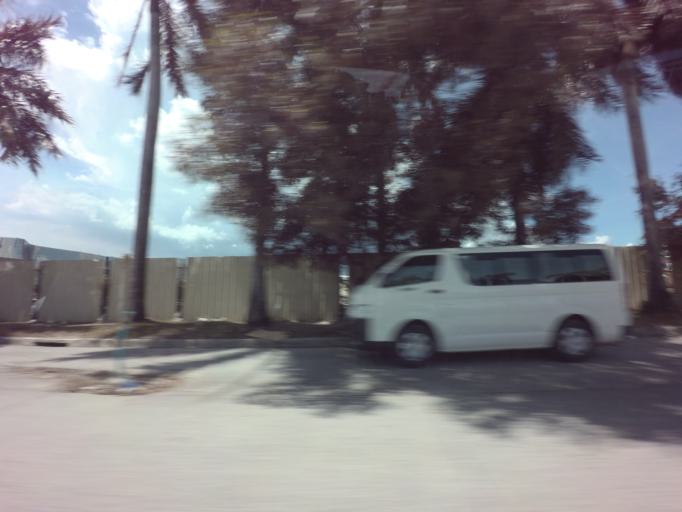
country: PH
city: Sambayanihan People's Village
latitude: 14.5088
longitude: 120.9819
